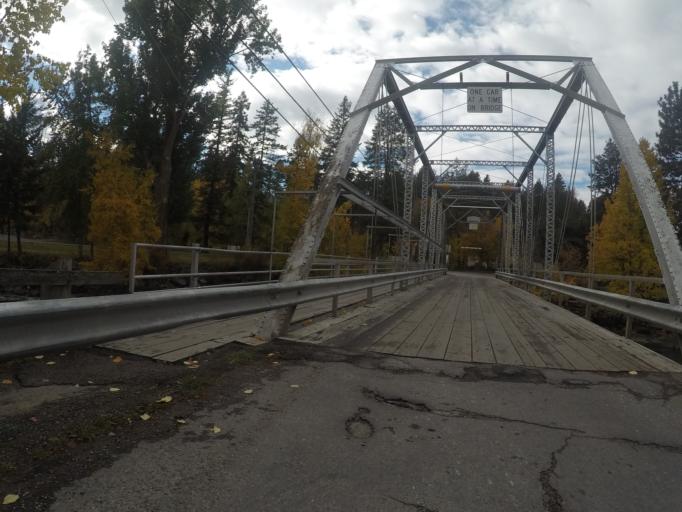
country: US
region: Montana
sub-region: Flathead County
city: Bigfork
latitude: 48.0594
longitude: -114.0725
